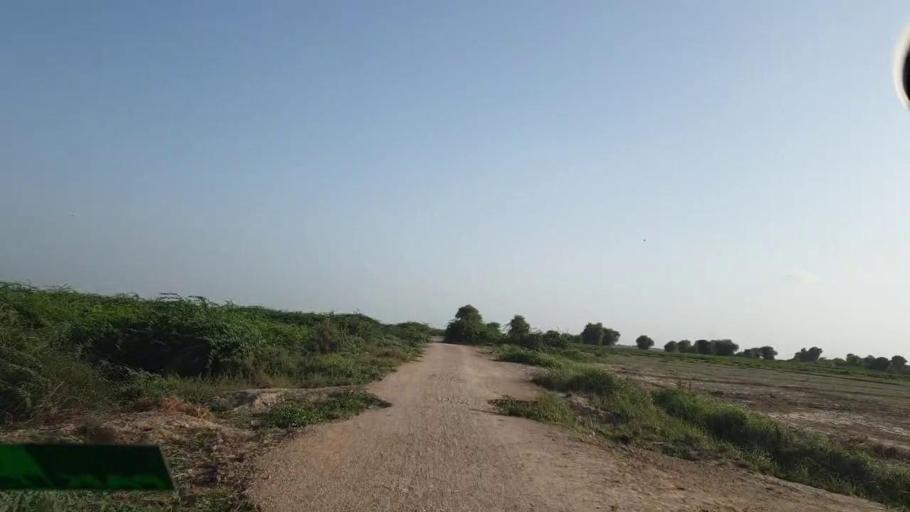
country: PK
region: Sindh
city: Naukot
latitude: 24.7219
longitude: 69.2516
